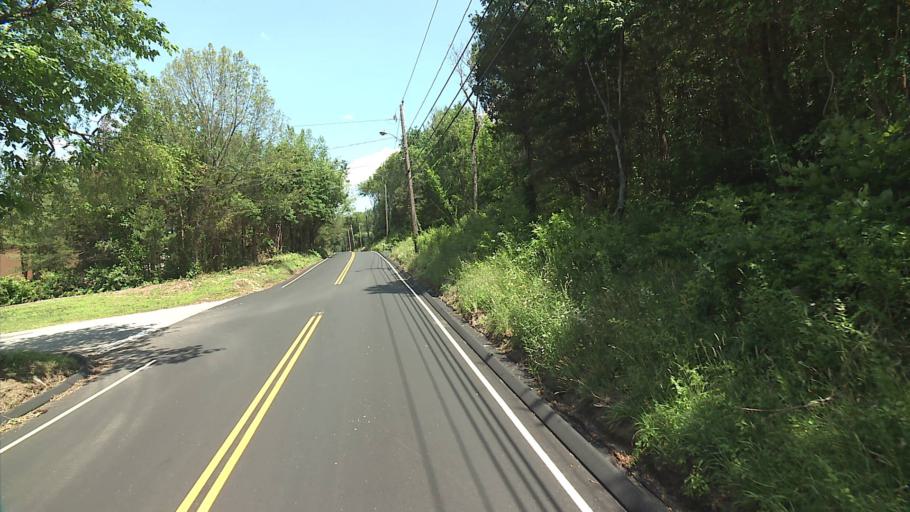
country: US
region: Connecticut
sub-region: New London County
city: Preston City
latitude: 41.5629
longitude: -71.8920
